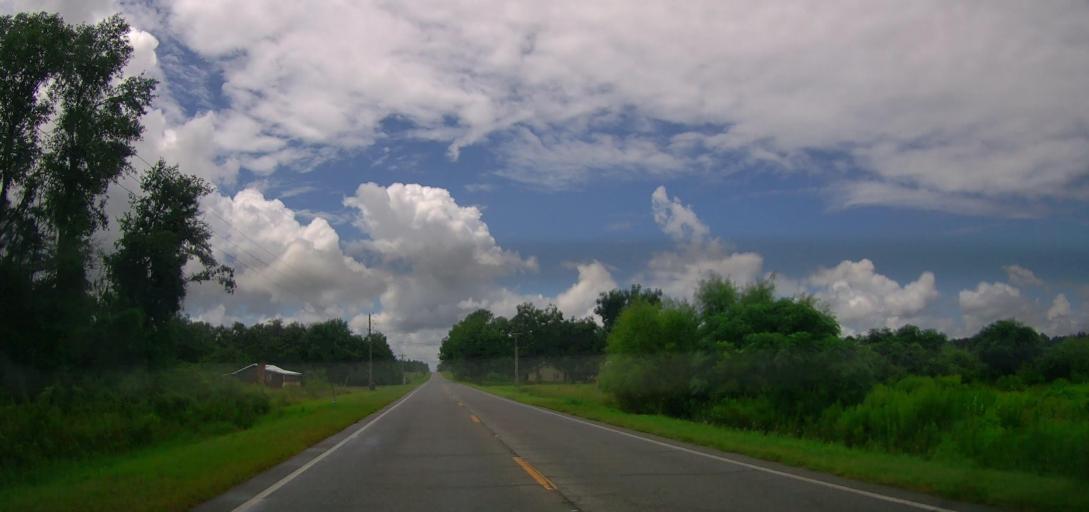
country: US
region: Georgia
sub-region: Wilcox County
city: Rochelle
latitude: 32.0358
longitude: -83.5943
